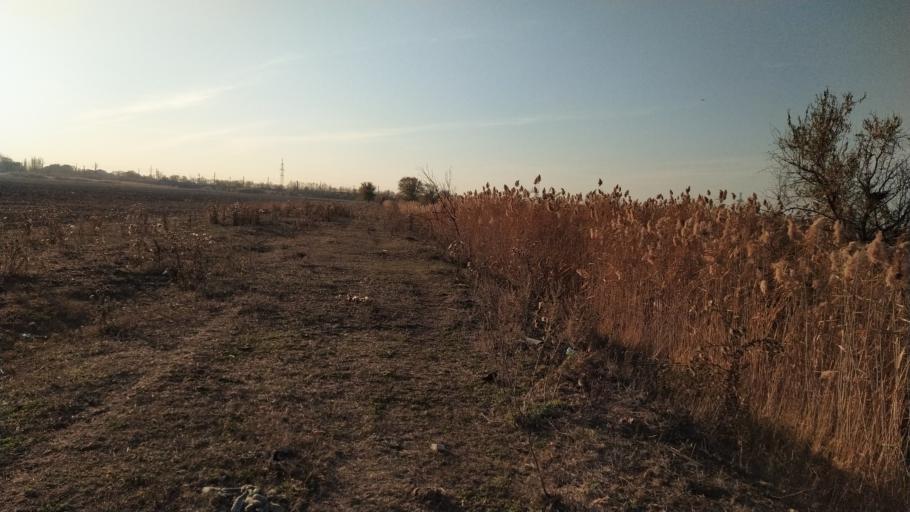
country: RU
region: Rostov
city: Bataysk
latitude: 47.1215
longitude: 39.7207
